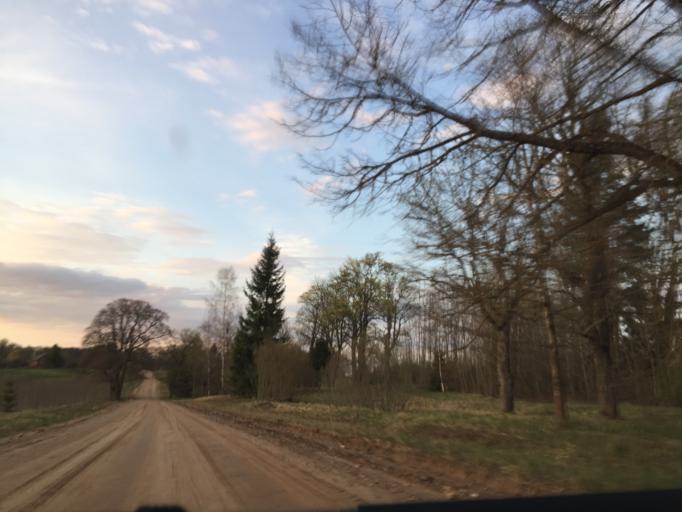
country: LV
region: Gulbenes Rajons
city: Gulbene
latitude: 57.2647
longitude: 26.9264
